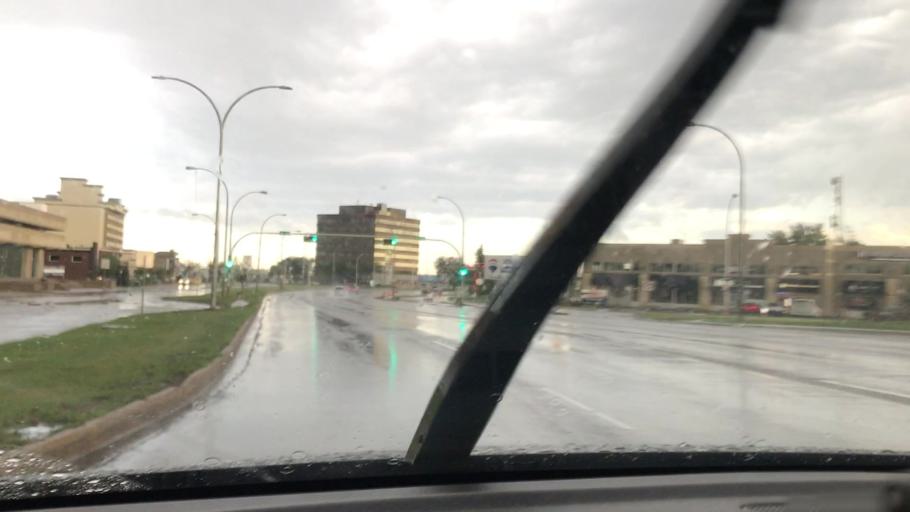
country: CA
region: Alberta
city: Edmonton
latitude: 53.4929
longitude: -113.4971
